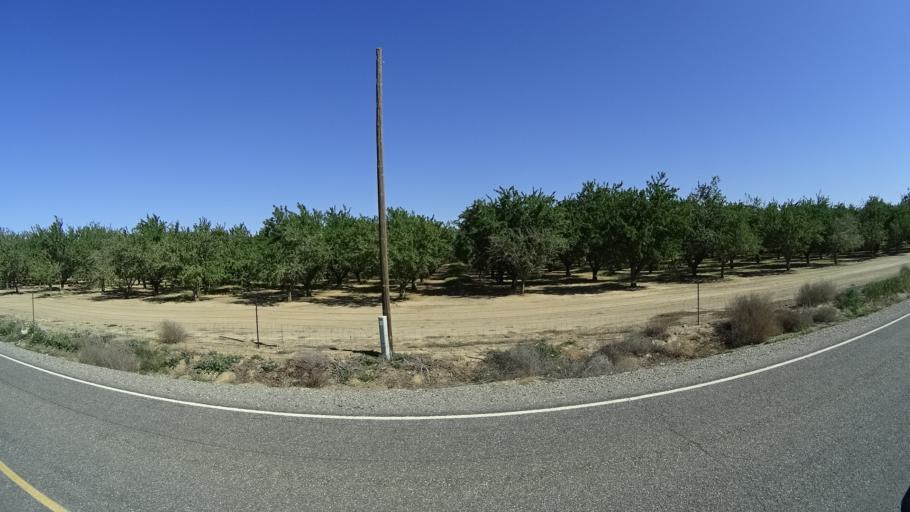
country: US
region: California
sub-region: Glenn County
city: Willows
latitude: 39.6237
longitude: -122.1355
